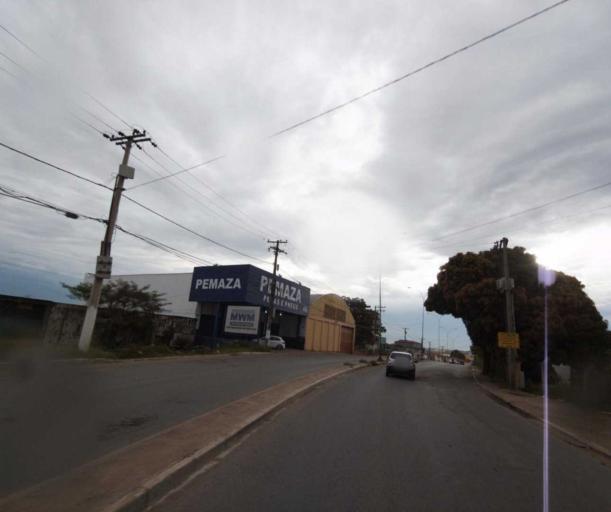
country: BR
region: Mato Grosso
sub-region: Varzea Grande
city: Varzea Grande
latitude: -15.6482
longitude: -56.1435
